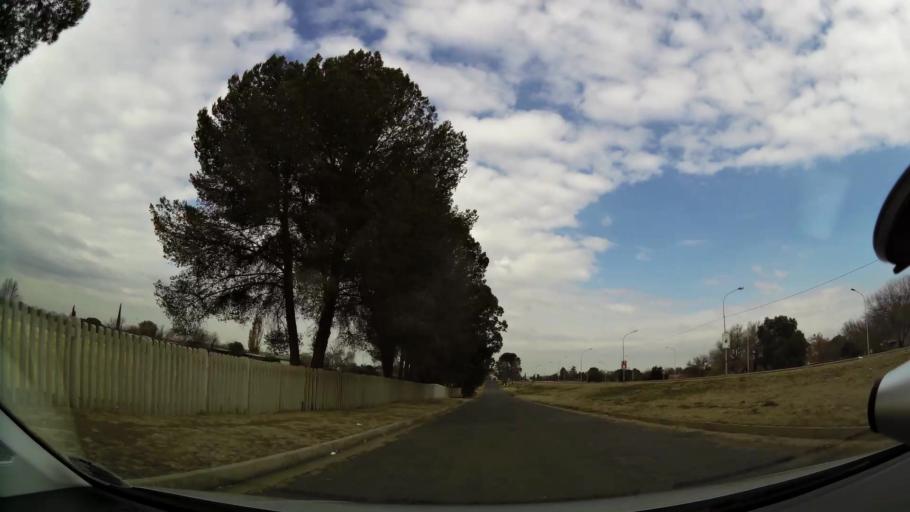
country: ZA
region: Orange Free State
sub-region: Fezile Dabi District Municipality
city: Kroonstad
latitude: -27.6398
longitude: 27.2339
